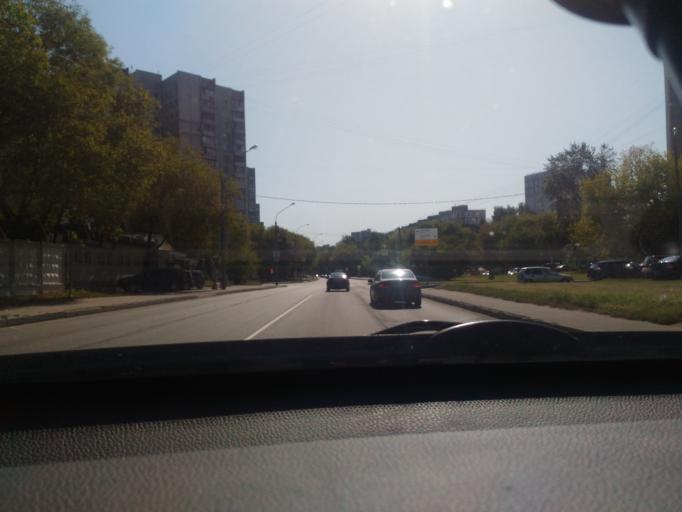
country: RU
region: Moscow
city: Vatutino
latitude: 55.8859
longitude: 37.6857
